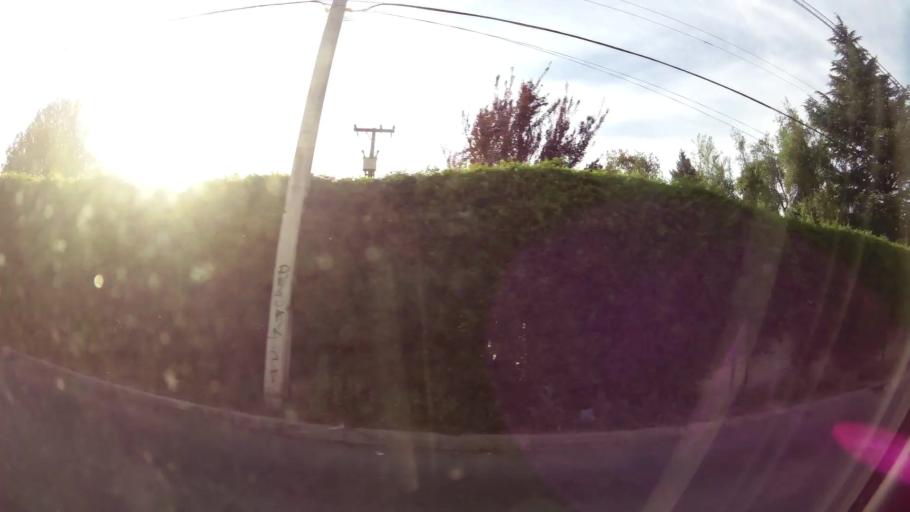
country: CL
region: Santiago Metropolitan
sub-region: Provincia de Maipo
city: San Bernardo
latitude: -33.5623
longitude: -70.7736
